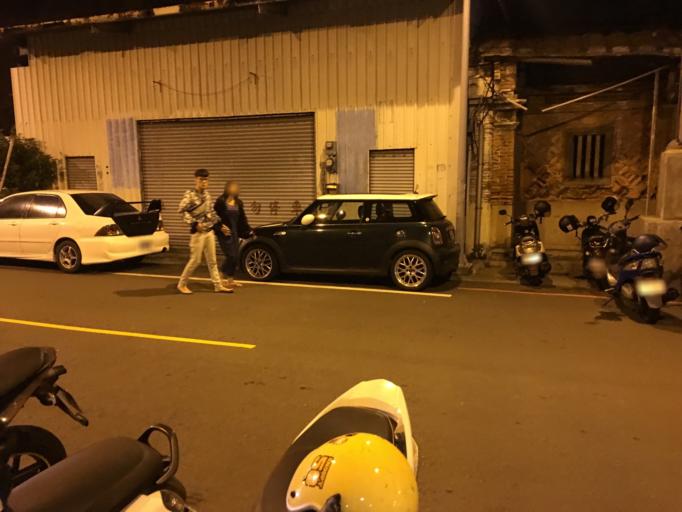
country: TW
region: Taiwan
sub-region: Hsinchu
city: Hsinchu
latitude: 24.8094
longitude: 120.9654
